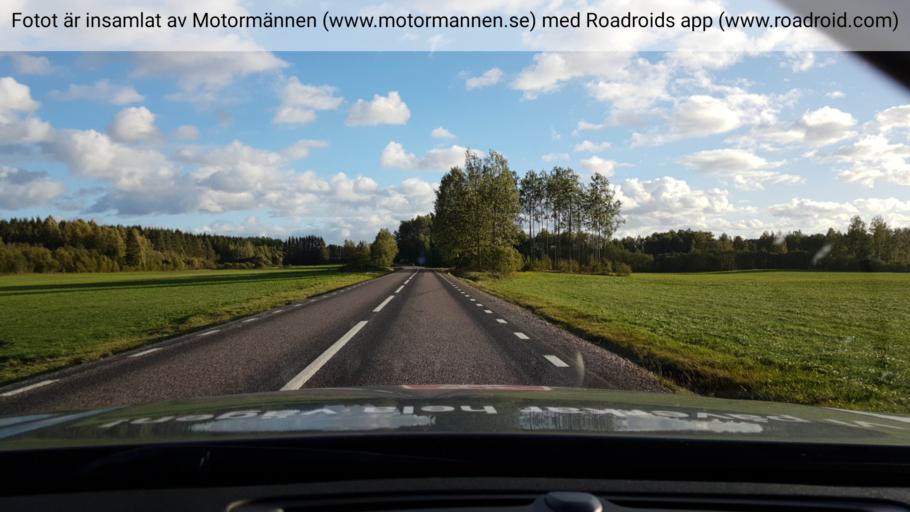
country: SE
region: Vaermland
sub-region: Karlstads Kommun
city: Molkom
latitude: 59.7067
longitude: 13.6803
